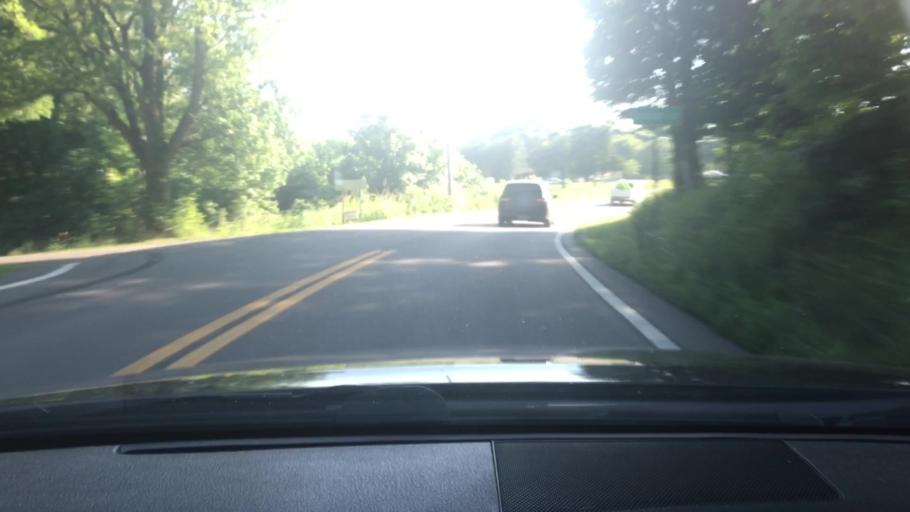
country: US
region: Tennessee
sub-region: Cheatham County
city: Ashland City
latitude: 36.2862
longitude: -87.1686
